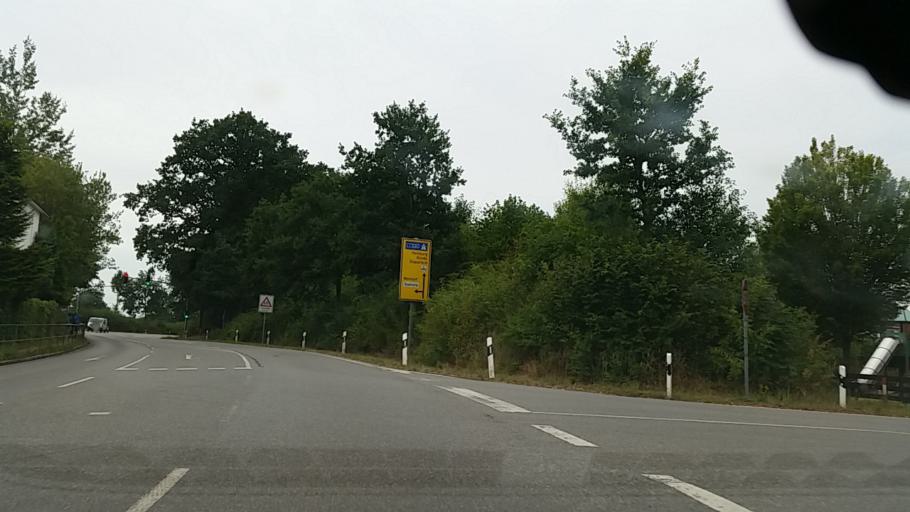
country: DE
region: Schleswig-Holstein
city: Reinbek
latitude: 53.5296
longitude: 10.2588
